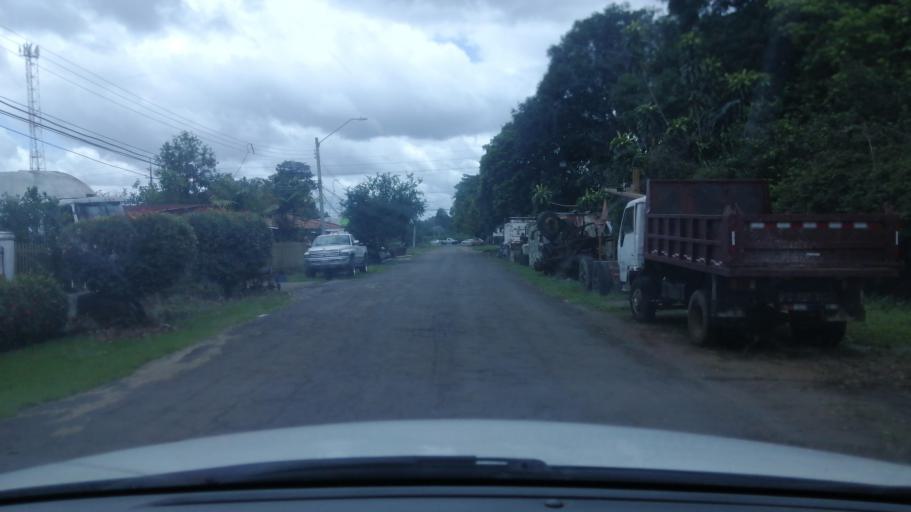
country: PA
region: Chiriqui
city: David
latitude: 8.4440
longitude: -82.4287
